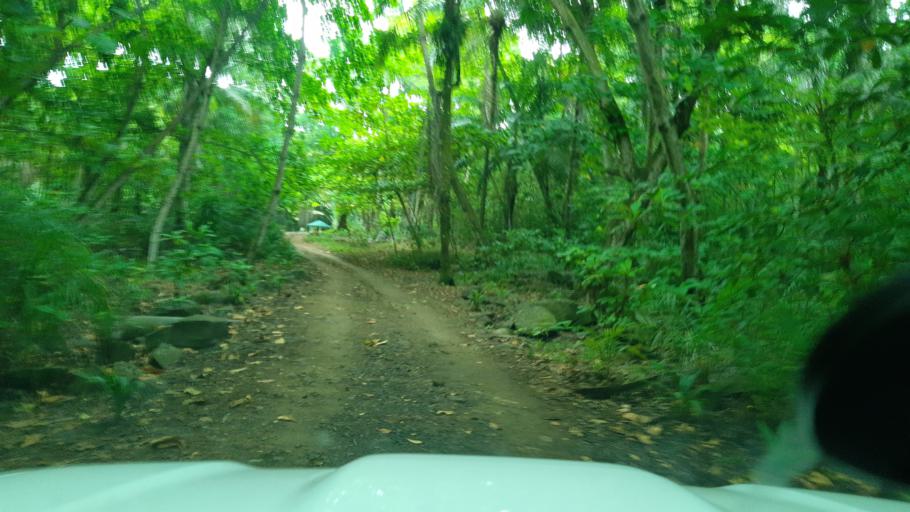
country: ST
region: Sao Tome Island
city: Sao Tome
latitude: 0.2446
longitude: 6.7454
